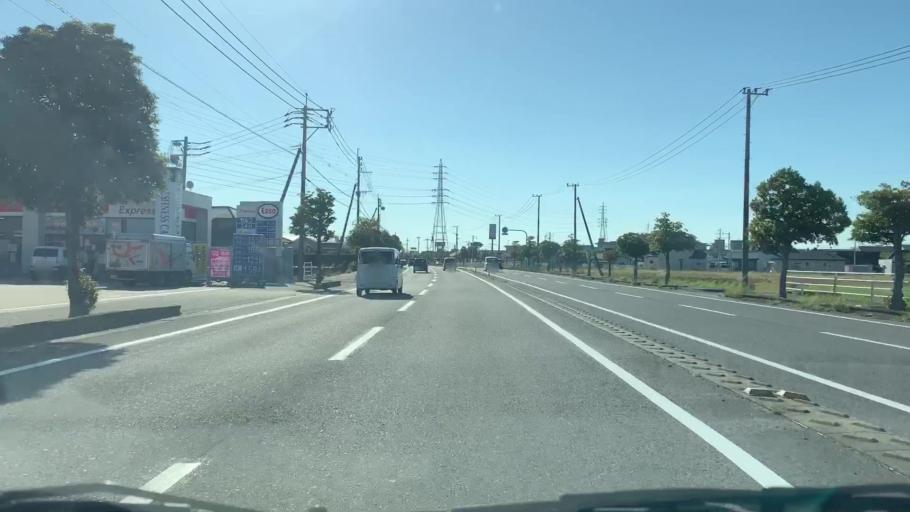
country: JP
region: Saga Prefecture
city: Saga-shi
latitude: 33.2979
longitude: 130.2814
